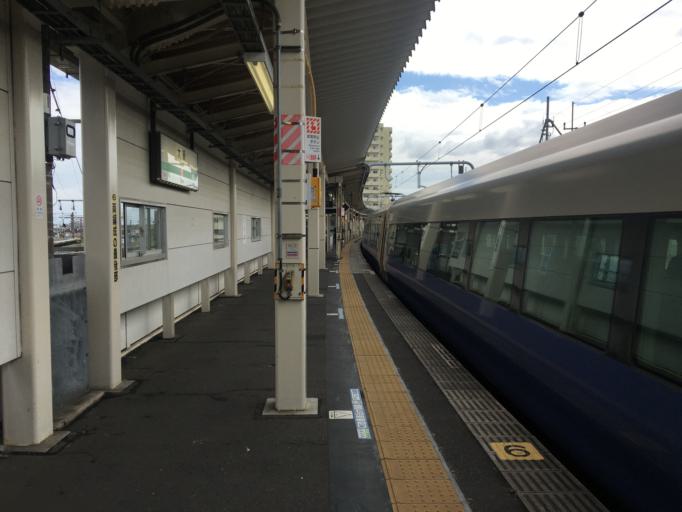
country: JP
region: Chiba
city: Oami
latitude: 35.5230
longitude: 140.3103
